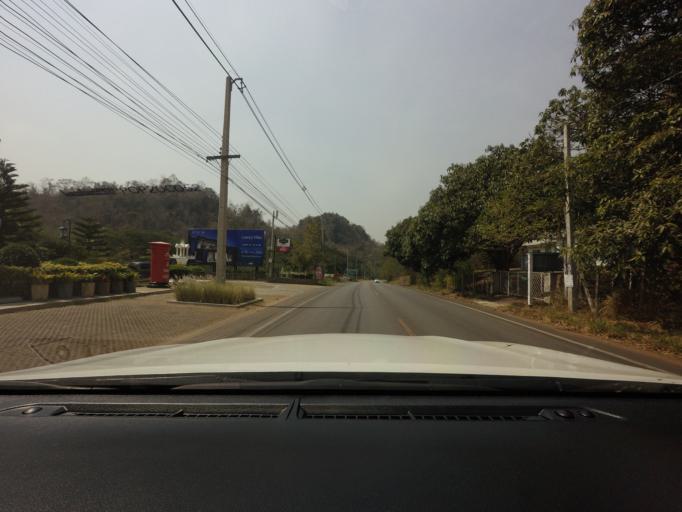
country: TH
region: Sara Buri
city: Muak Lek
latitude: 14.5737
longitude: 101.2814
